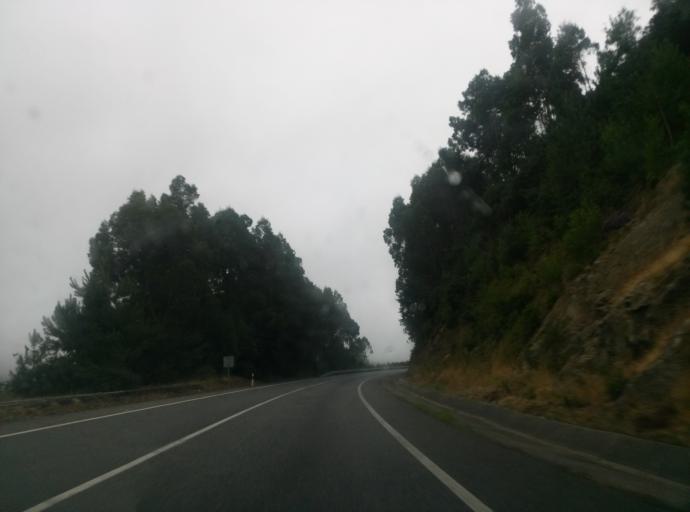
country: ES
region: Galicia
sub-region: Provincia de Lugo
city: Viveiro
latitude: 43.5632
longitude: -7.6433
